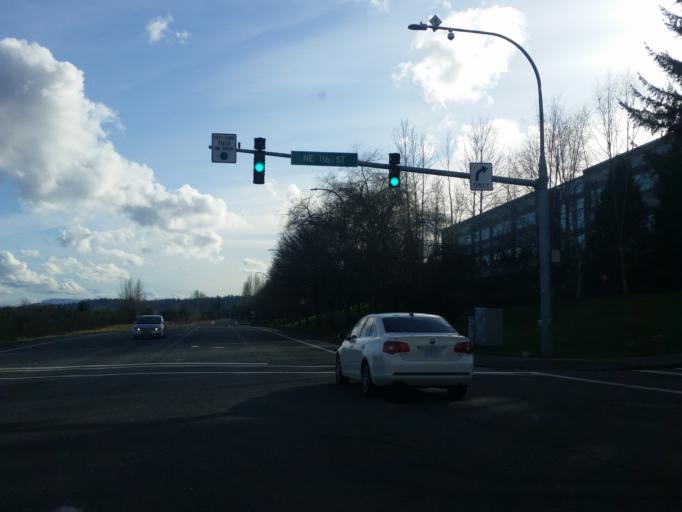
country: US
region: Washington
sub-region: King County
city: Kingsgate
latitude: 47.7043
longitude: -122.1533
